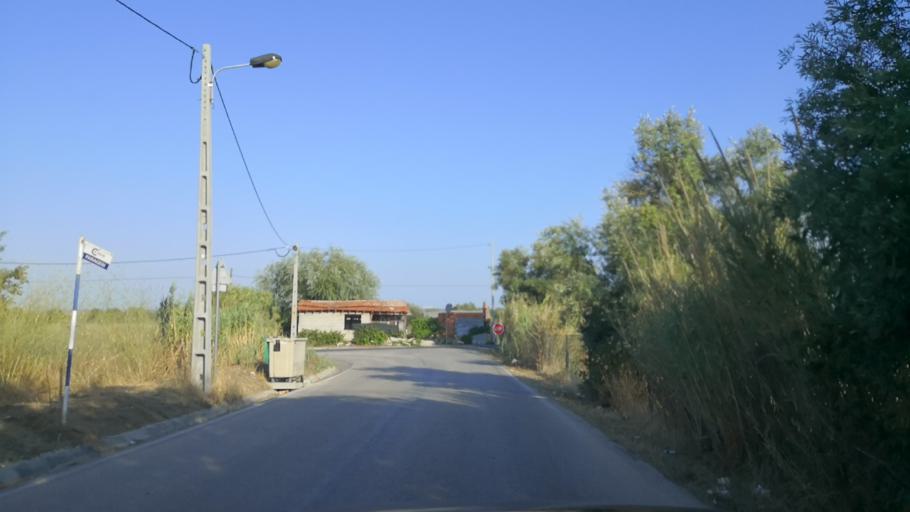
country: PT
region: Santarem
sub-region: Santarem
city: Santarem
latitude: 39.2543
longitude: -8.6721
